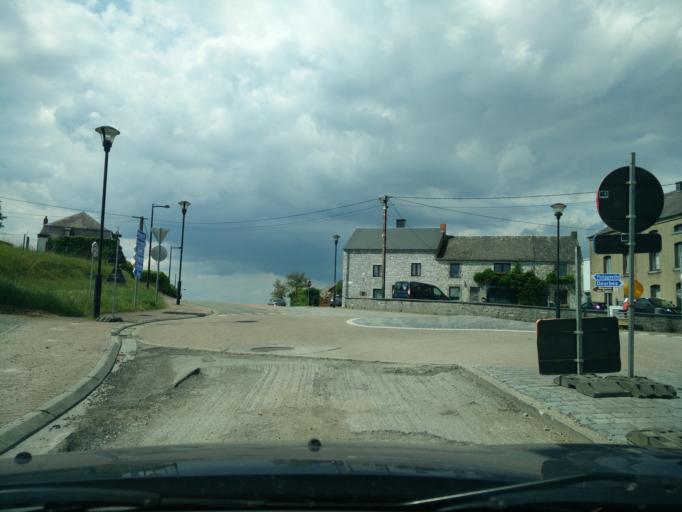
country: BE
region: Wallonia
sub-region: Province de Namur
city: Couvin
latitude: 50.0788
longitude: 4.5492
